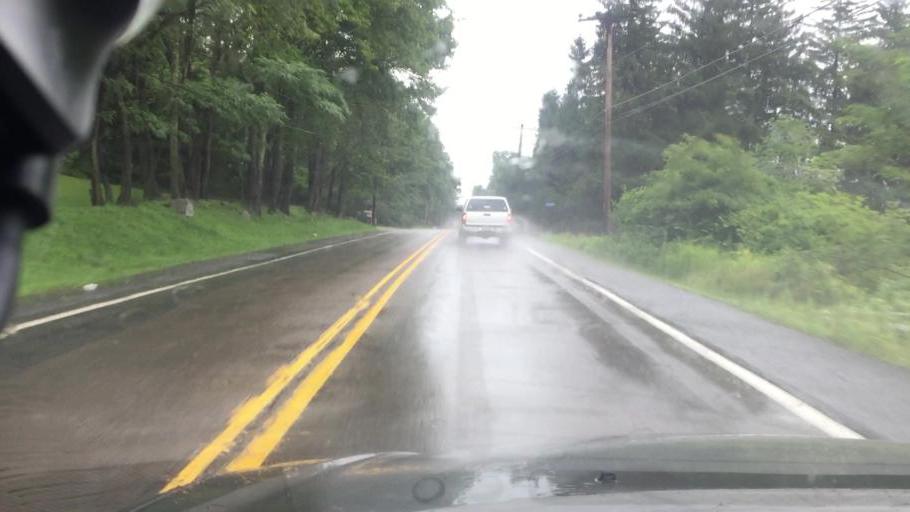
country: US
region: Pennsylvania
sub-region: Luzerne County
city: White Haven
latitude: 41.0433
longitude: -75.8055
